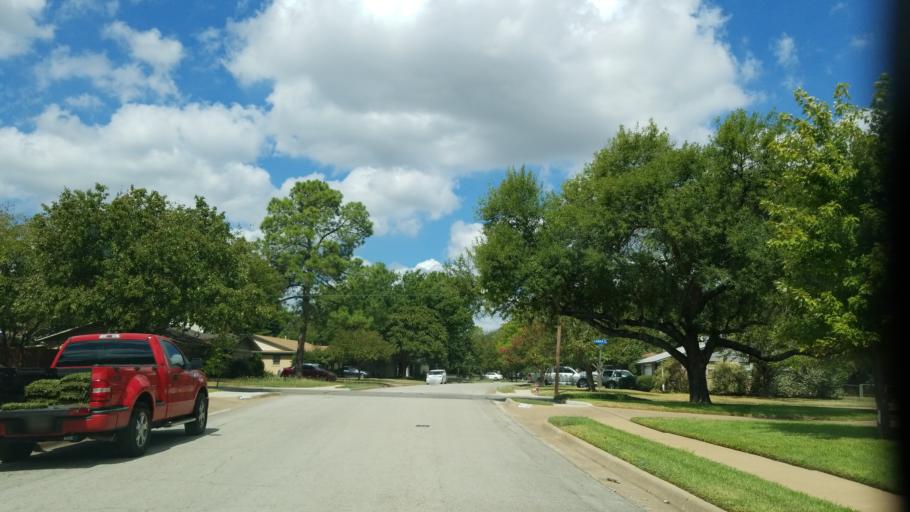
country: US
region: Texas
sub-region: Tarrant County
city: Euless
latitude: 32.8486
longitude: -97.0936
